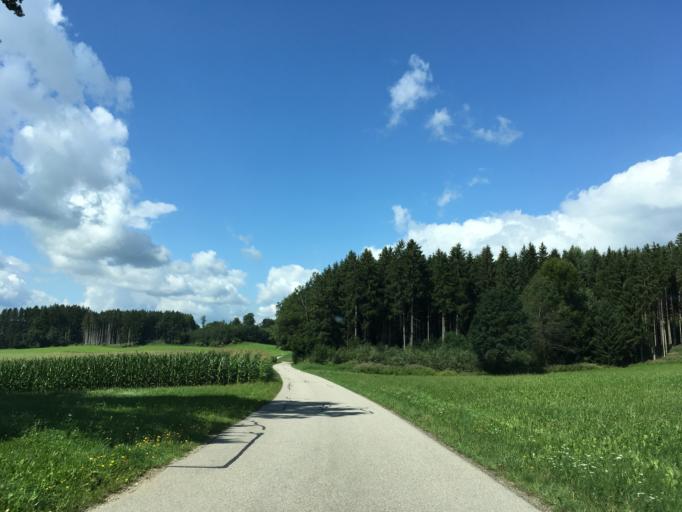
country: DE
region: Bavaria
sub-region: Upper Bavaria
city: Pittenhart
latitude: 47.9732
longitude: 12.3677
